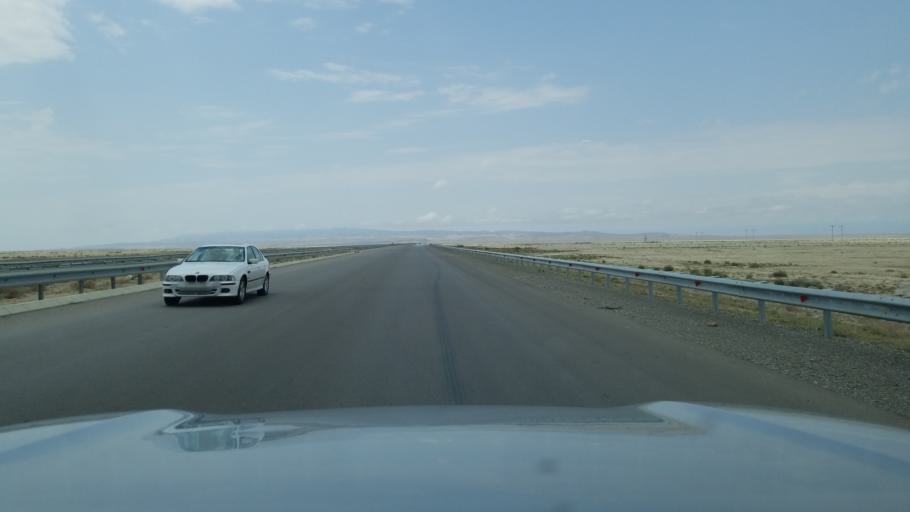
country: TM
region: Balkan
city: Gazanjyk
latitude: 39.2760
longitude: 55.2636
